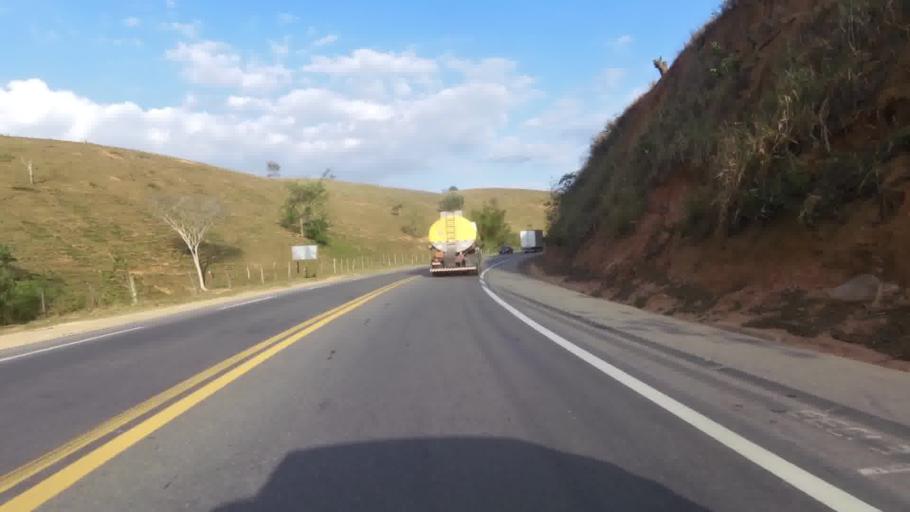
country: BR
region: Espirito Santo
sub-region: Rio Novo Do Sul
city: Rio Novo do Sul
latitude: -20.8932
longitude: -41.0271
